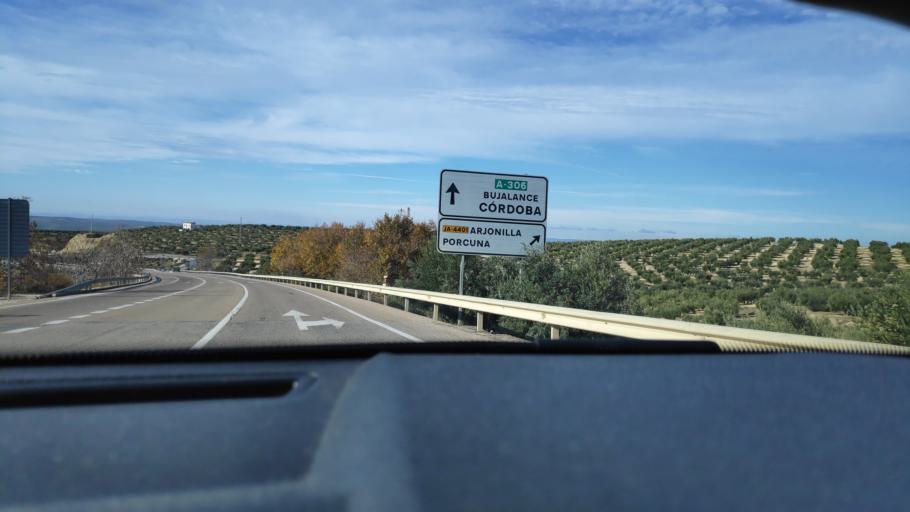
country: ES
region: Andalusia
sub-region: Provincia de Jaen
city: Porcuna
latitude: 37.8794
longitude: -4.1772
